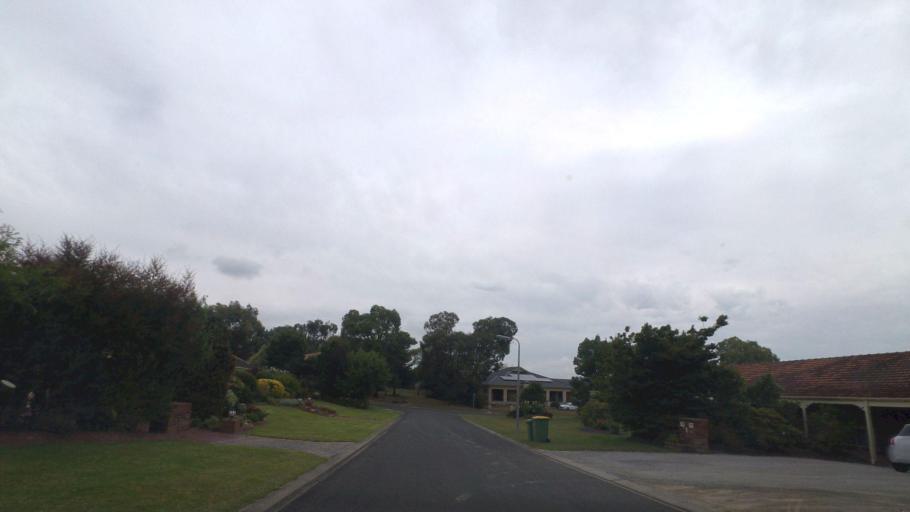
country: AU
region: Victoria
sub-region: Yarra Ranges
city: Kilsyth
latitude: -37.7963
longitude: 145.3360
